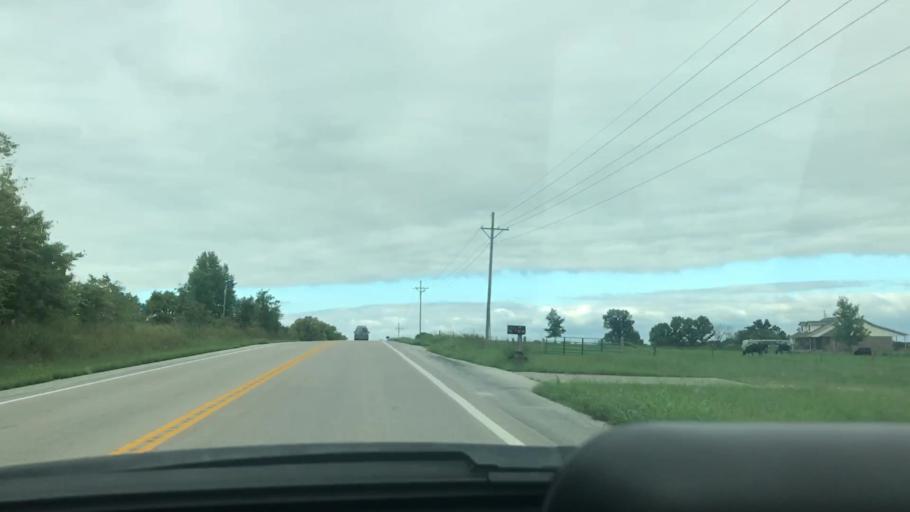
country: US
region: Missouri
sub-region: Hickory County
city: Hermitage
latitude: 37.8727
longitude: -93.1807
